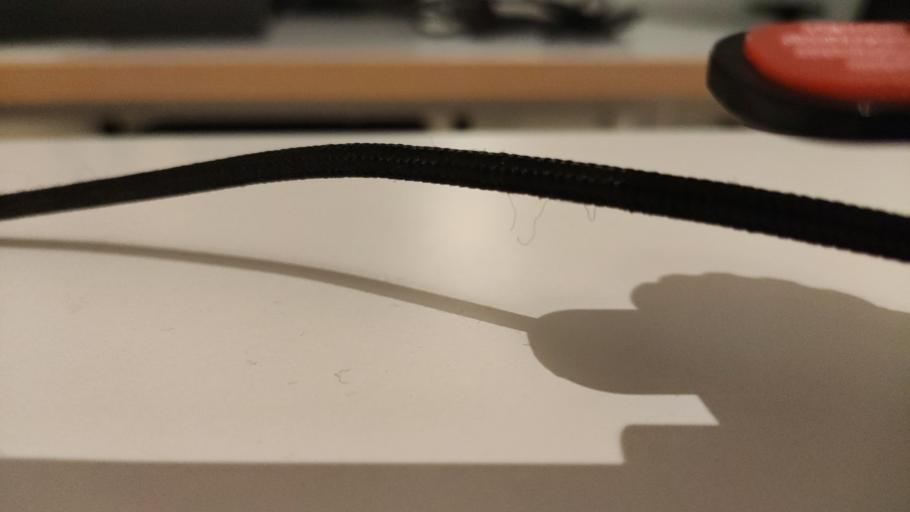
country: RU
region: Moskovskaya
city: Novoye
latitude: 55.6109
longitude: 38.9306
